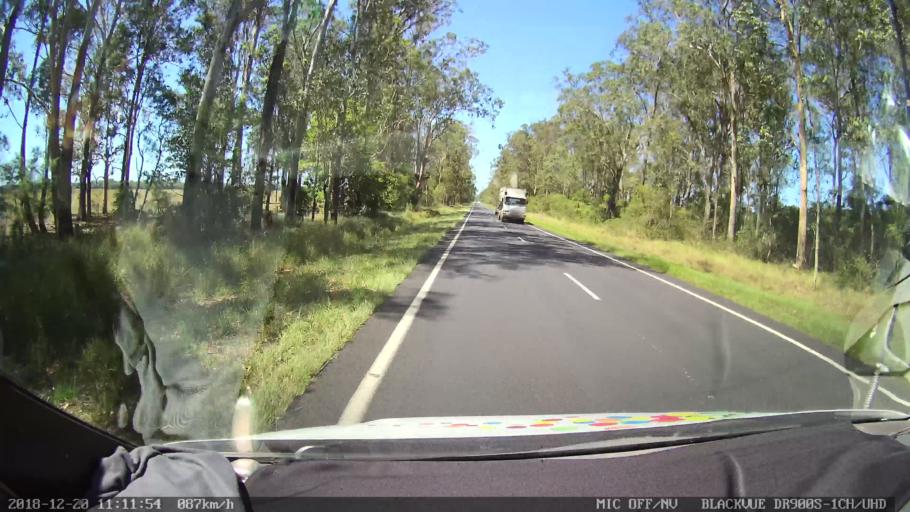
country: AU
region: New South Wales
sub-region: Richmond Valley
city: Casino
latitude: -28.9669
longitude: 153.0125
